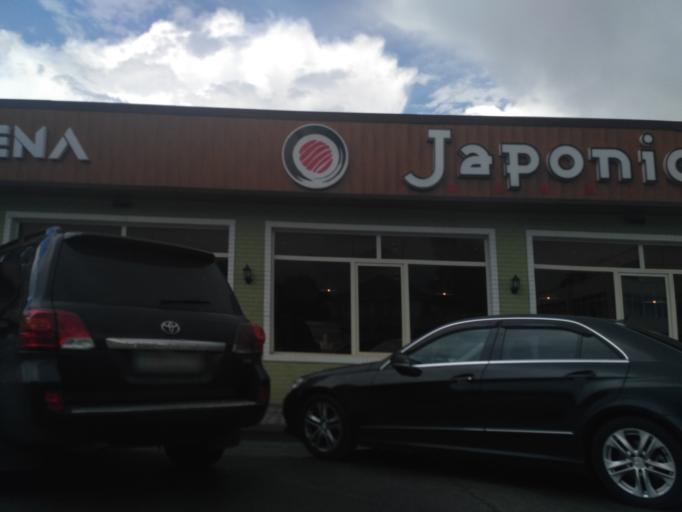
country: KZ
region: Almaty Oblysy
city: Burunday
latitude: 43.2025
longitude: 76.6225
